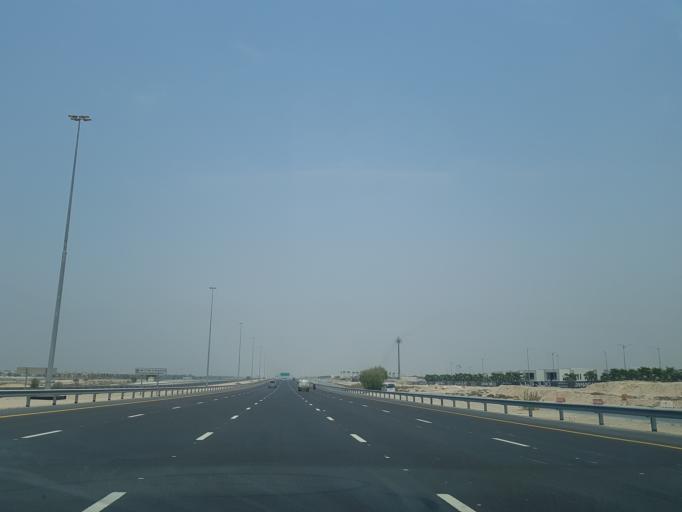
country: AE
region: Dubai
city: Dubai
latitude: 25.0270
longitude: 55.2453
